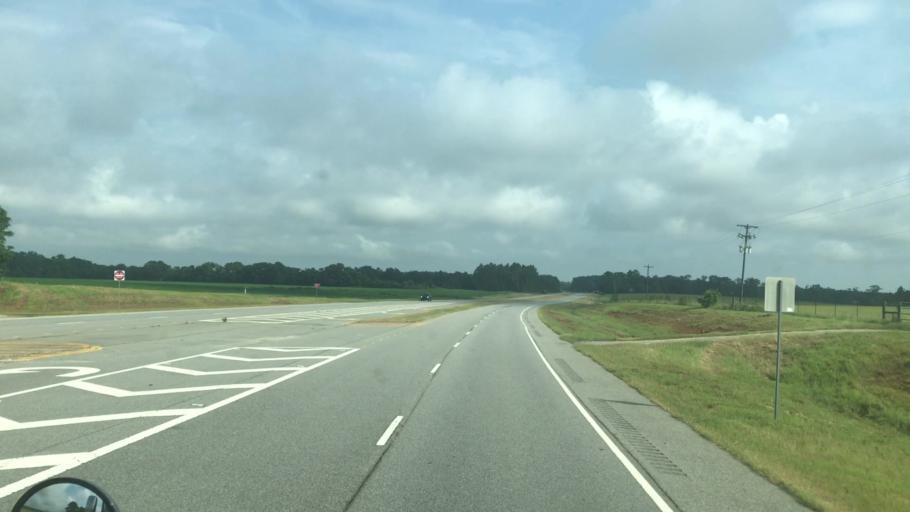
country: US
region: Georgia
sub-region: Miller County
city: Colquitt
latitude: 31.2164
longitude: -84.7776
